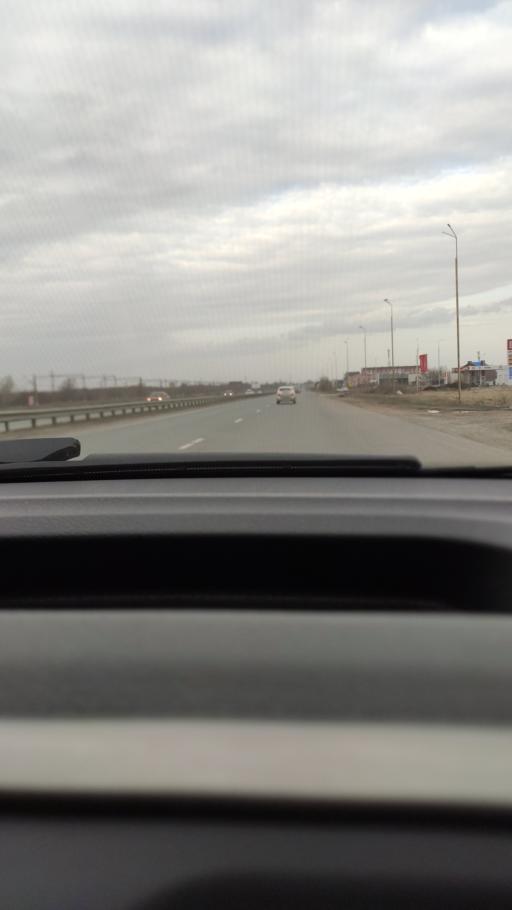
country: RU
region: Samara
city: Tol'yatti
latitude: 53.5698
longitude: 49.3798
